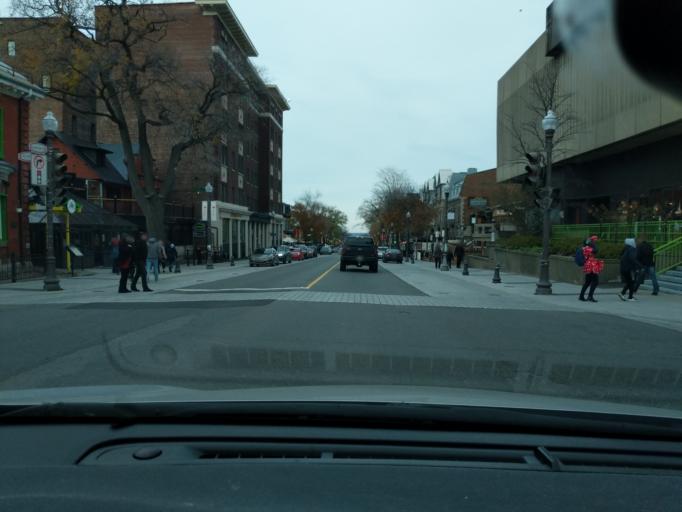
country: CA
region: Quebec
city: Quebec
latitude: 46.8055
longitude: -71.2179
